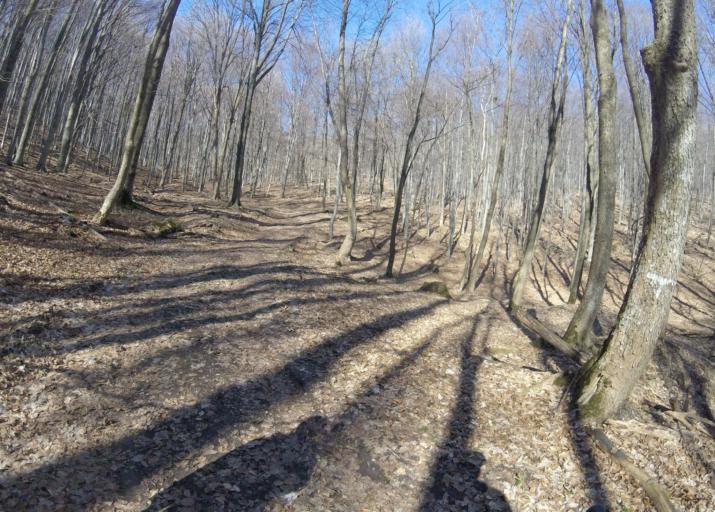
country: HU
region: Heves
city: Szilvasvarad
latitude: 48.0548
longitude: 20.4305
